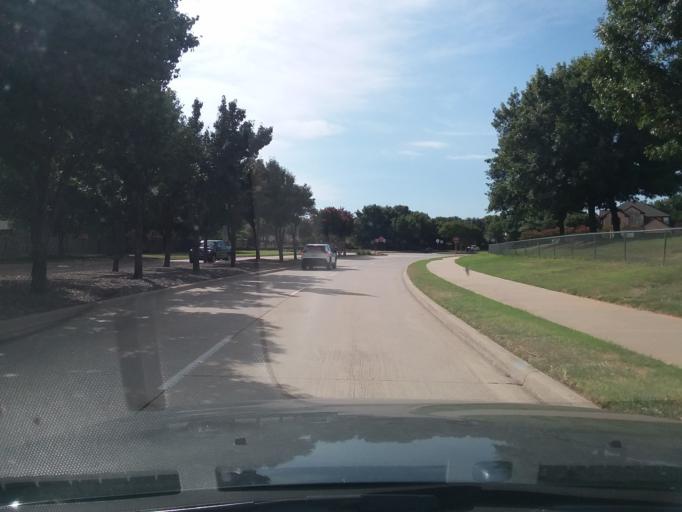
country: US
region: Texas
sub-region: Denton County
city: Flower Mound
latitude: 33.0310
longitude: -97.0918
